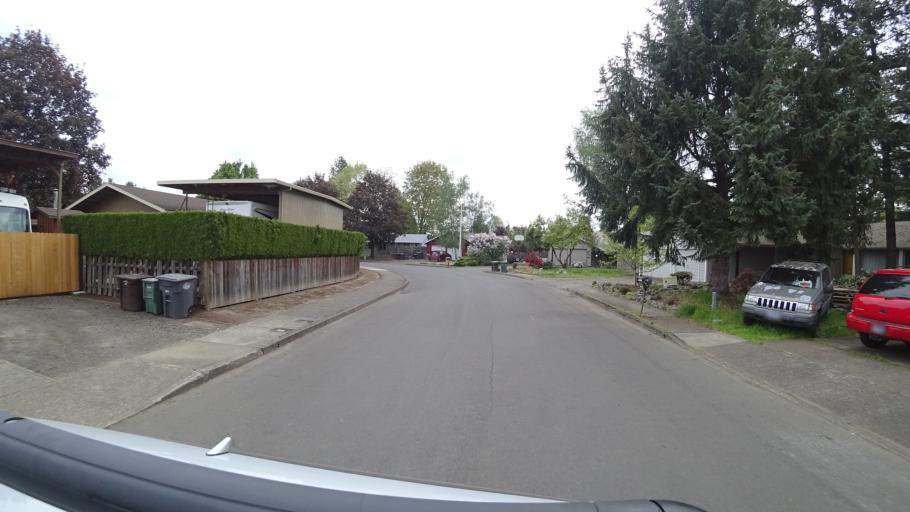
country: US
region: Oregon
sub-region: Washington County
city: Hillsboro
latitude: 45.5335
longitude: -122.9747
